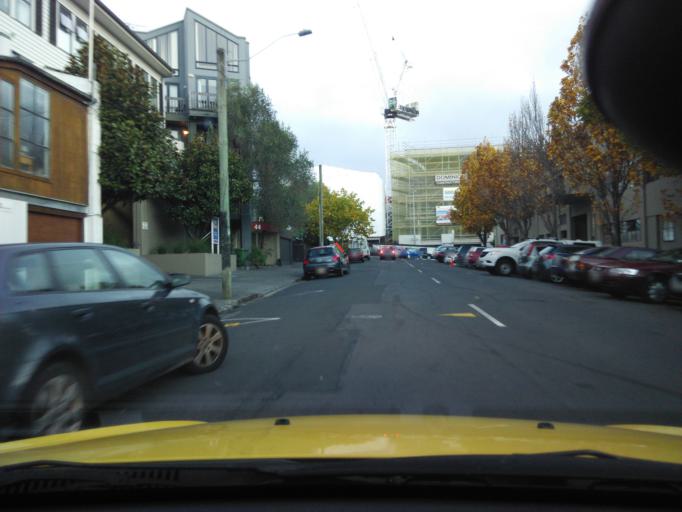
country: NZ
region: Auckland
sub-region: Auckland
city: Auckland
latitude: -36.8628
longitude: 174.7601
